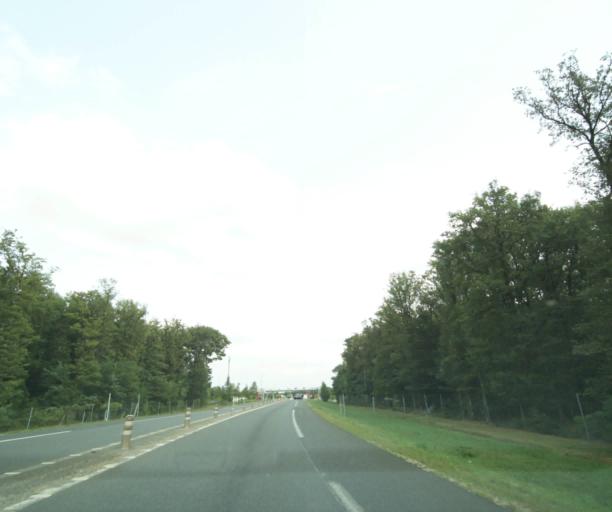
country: FR
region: Centre
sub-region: Departement d'Indre-et-Loire
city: Esvres
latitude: 47.3078
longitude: 0.7928
